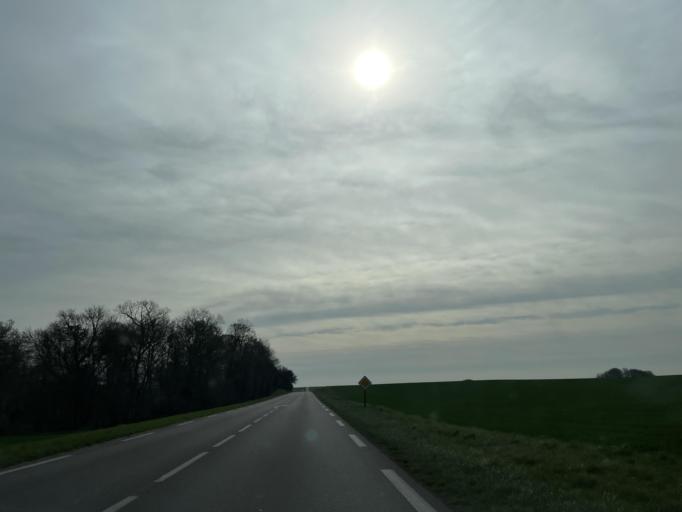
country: FR
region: Ile-de-France
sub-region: Departement de Seine-et-Marne
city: Sainte-Colombe
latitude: 48.5823
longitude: 3.2403
